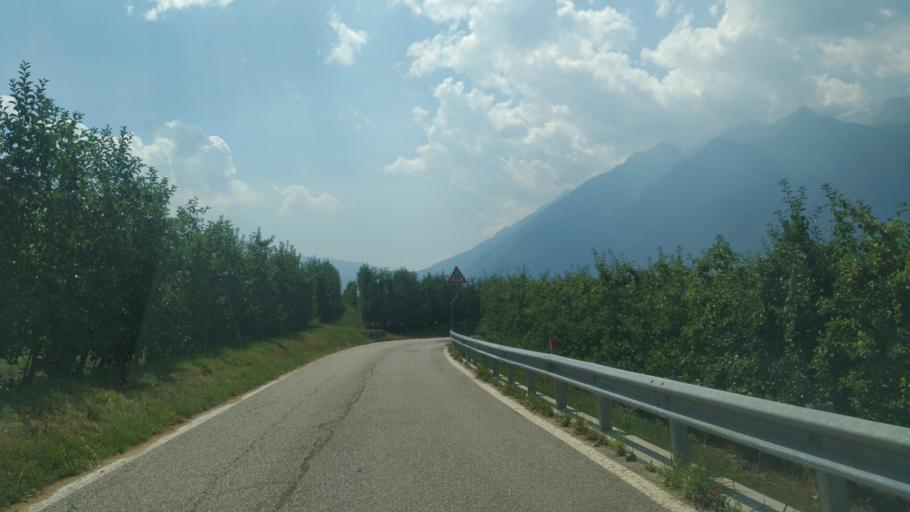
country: IT
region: Trentino-Alto Adige
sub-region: Provincia di Trento
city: Vigo di Ton
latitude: 46.2694
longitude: 11.0813
